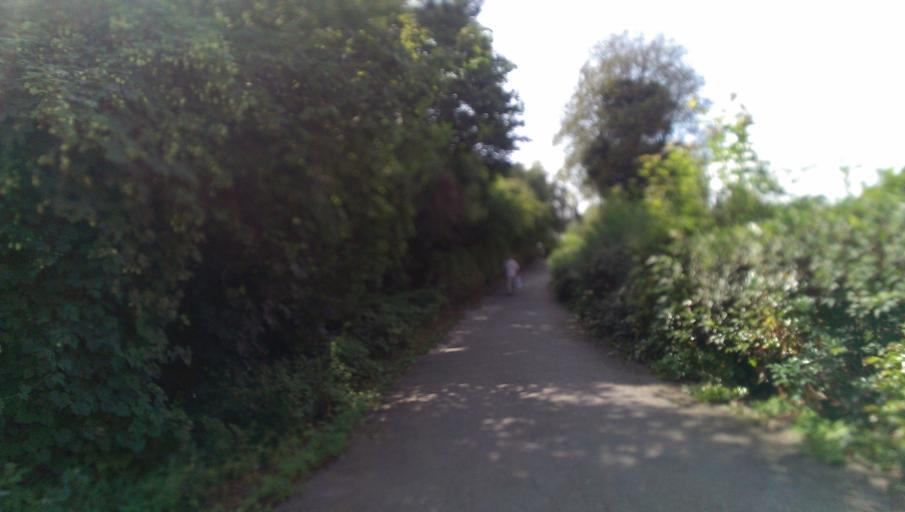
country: DE
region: Berlin
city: Mariendorf
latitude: 52.4482
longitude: 13.3688
